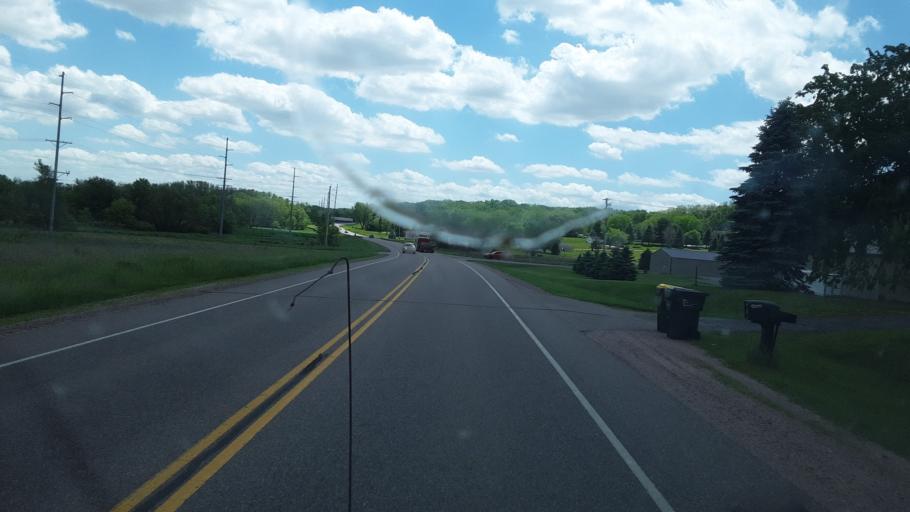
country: US
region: Wisconsin
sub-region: Sauk County
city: Reedsburg
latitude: 43.5634
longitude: -89.9725
